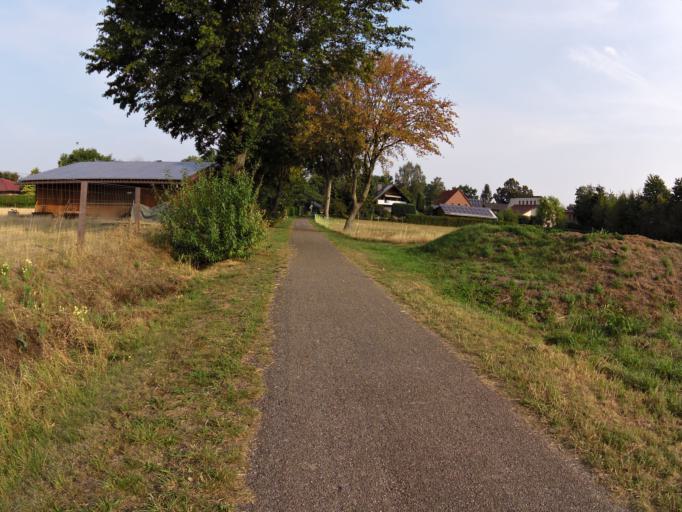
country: DE
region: Lower Saxony
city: Raddestorf
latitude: 52.4159
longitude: 8.9686
